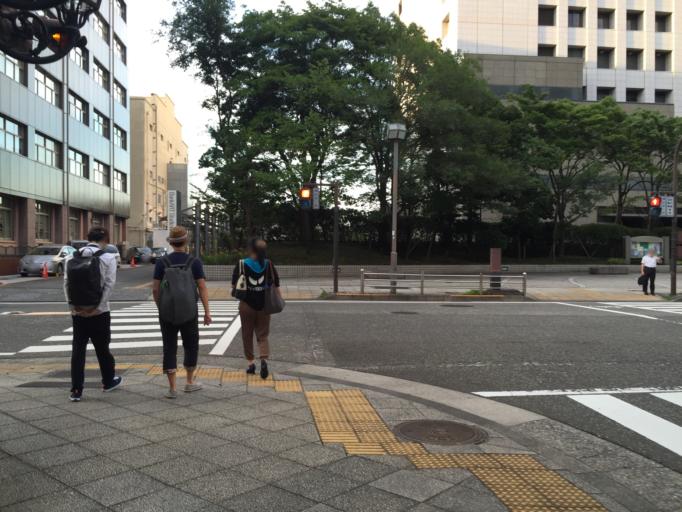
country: JP
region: Kanagawa
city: Yokohama
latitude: 35.4496
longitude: 139.6401
